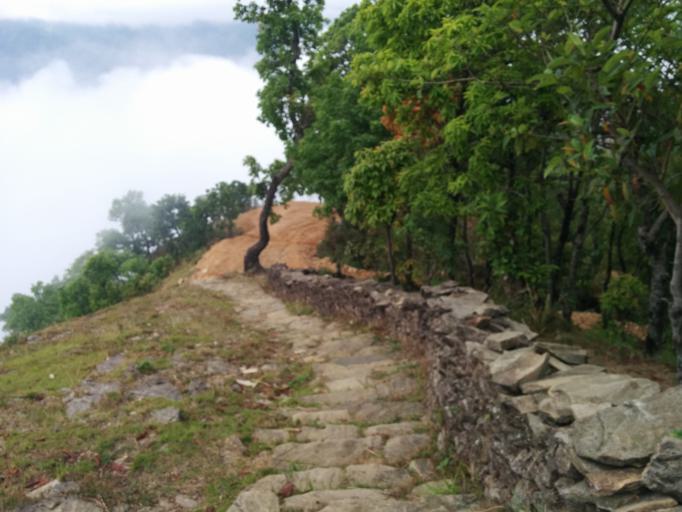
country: NP
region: Western Region
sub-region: Gandaki Zone
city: Pokhara
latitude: 28.2363
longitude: 83.9493
